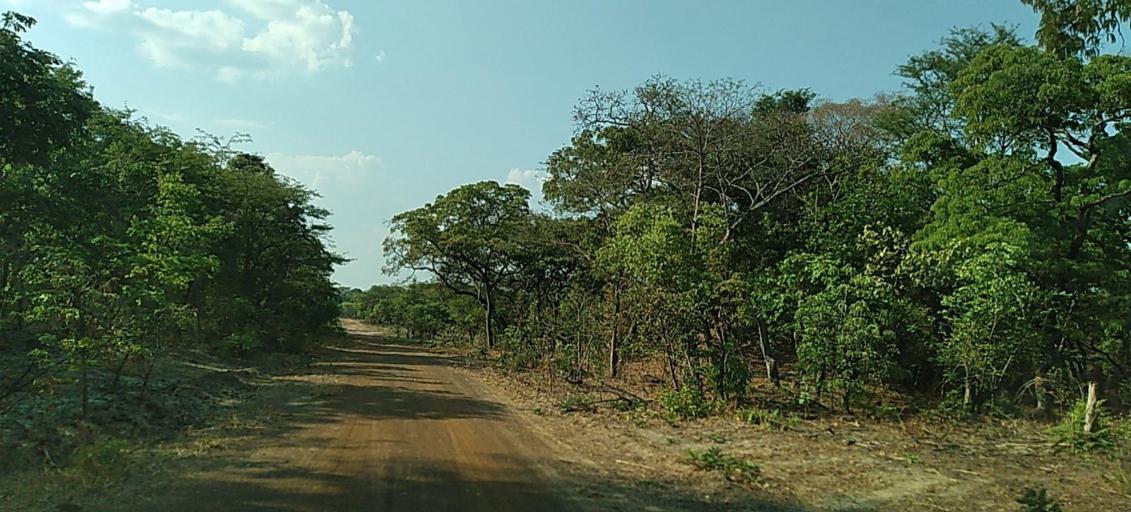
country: ZM
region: Copperbelt
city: Mpongwe
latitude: -13.4423
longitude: 28.0617
